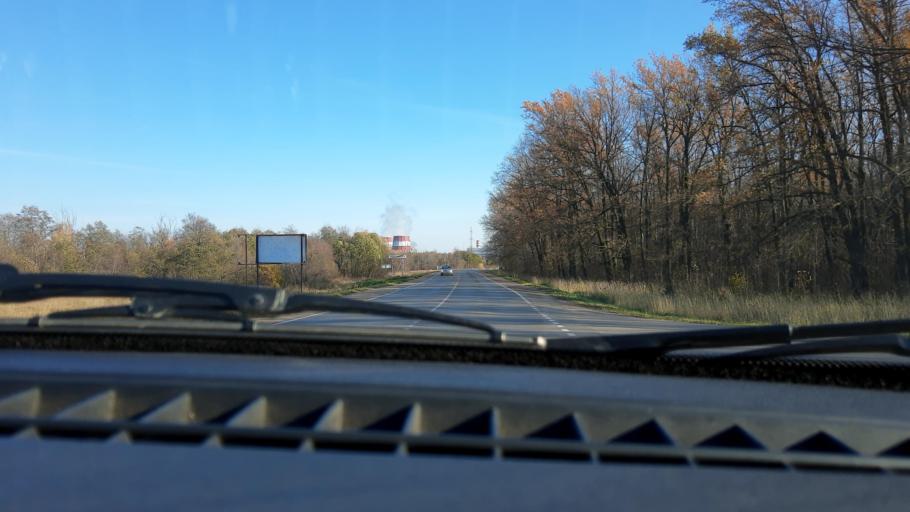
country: RU
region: Bashkortostan
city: Mikhaylovka
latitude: 54.8092
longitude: 55.8153
